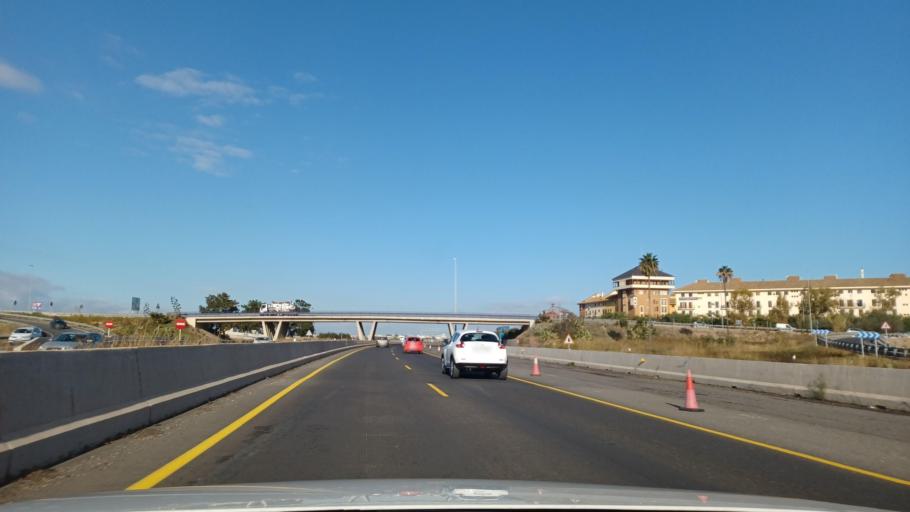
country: ES
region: Valencia
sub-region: Provincia de Valencia
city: Alboraya
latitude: 39.5073
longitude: -0.3256
